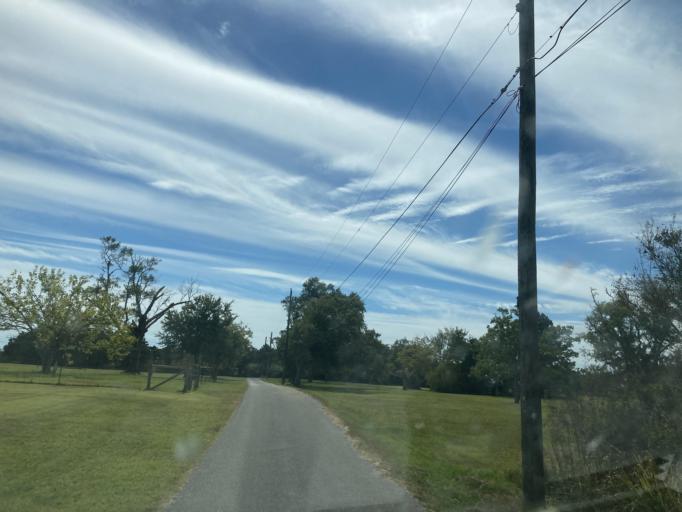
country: US
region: Mississippi
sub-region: Harrison County
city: D'Iberville
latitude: 30.4272
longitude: -88.8771
